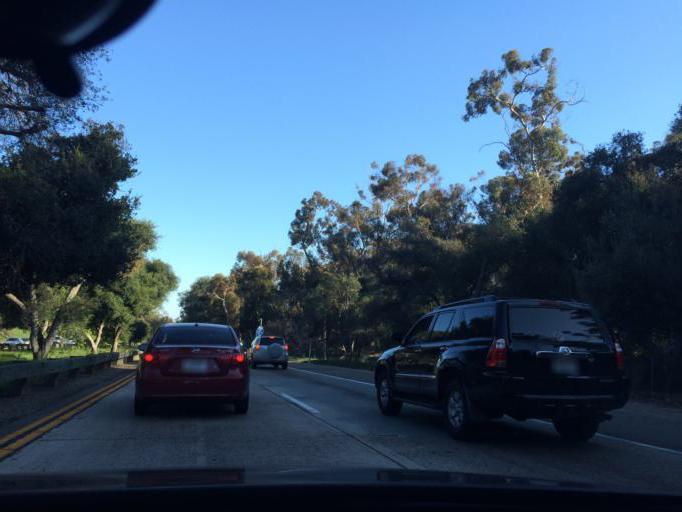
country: US
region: California
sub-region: San Diego County
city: San Diego
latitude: 32.7406
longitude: -117.1566
